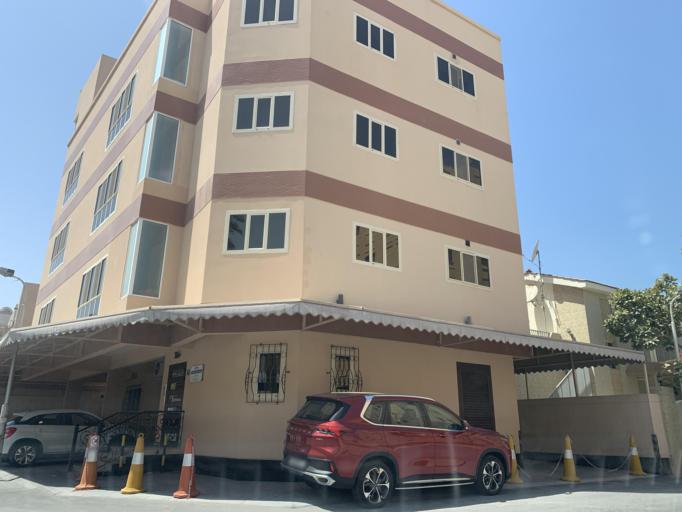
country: BH
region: Manama
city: Manama
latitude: 26.2108
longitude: 50.5672
